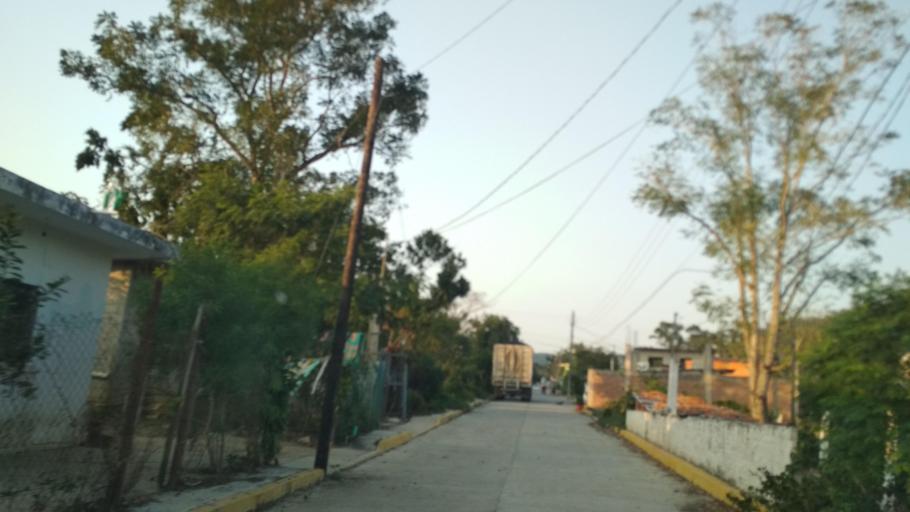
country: MM
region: Shan
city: Taunggyi
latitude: 20.4072
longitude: 97.3369
